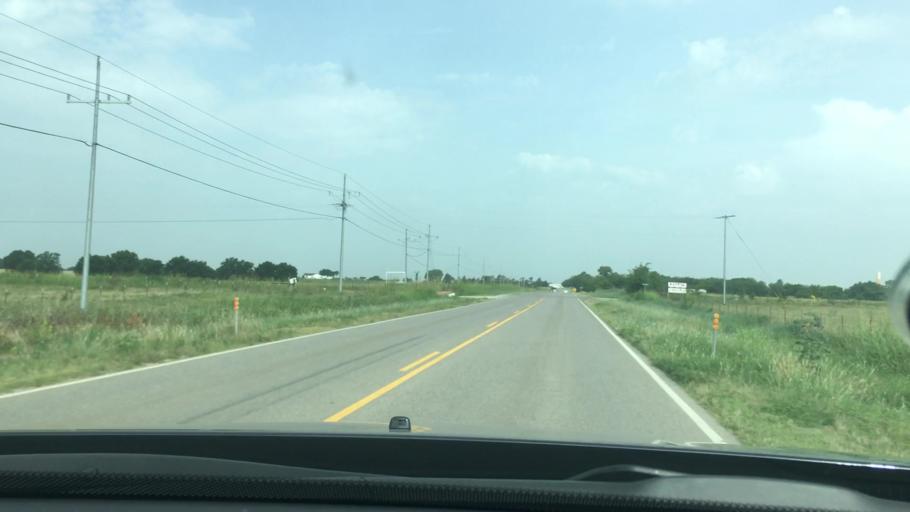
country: US
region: Oklahoma
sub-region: Pontotoc County
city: Ada
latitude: 34.7931
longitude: -96.8090
